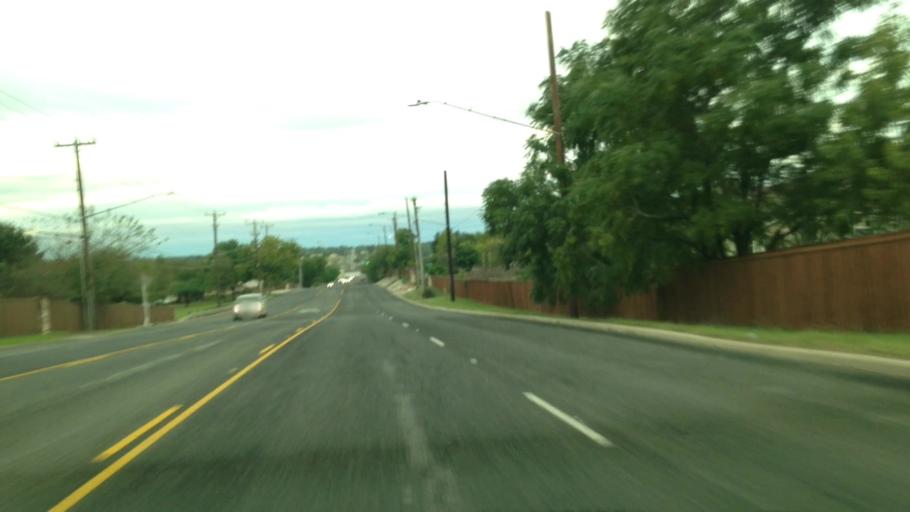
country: US
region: Texas
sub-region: Bexar County
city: Live Oak
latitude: 29.5569
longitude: -98.3584
